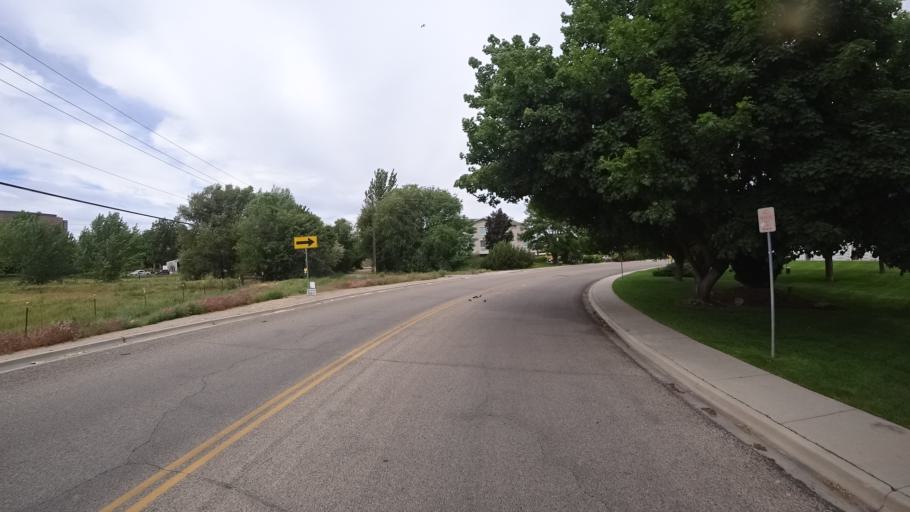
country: US
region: Idaho
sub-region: Ada County
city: Boise
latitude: 43.5754
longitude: -116.2116
